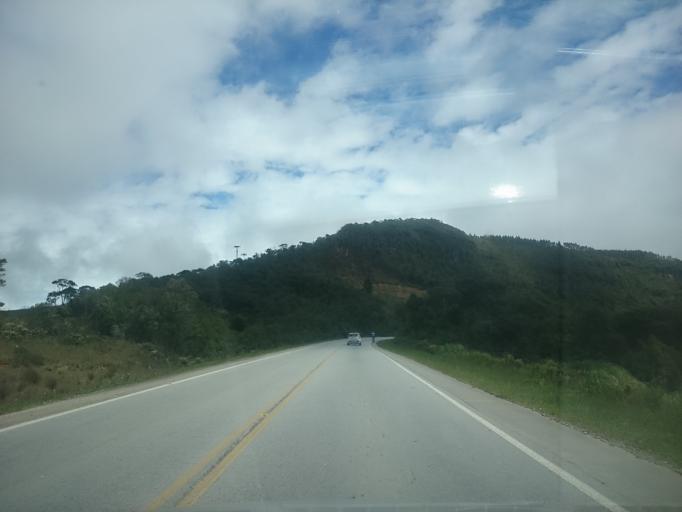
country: BR
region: Santa Catarina
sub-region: Anitapolis
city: Anitapolis
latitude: -27.6882
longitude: -49.1201
